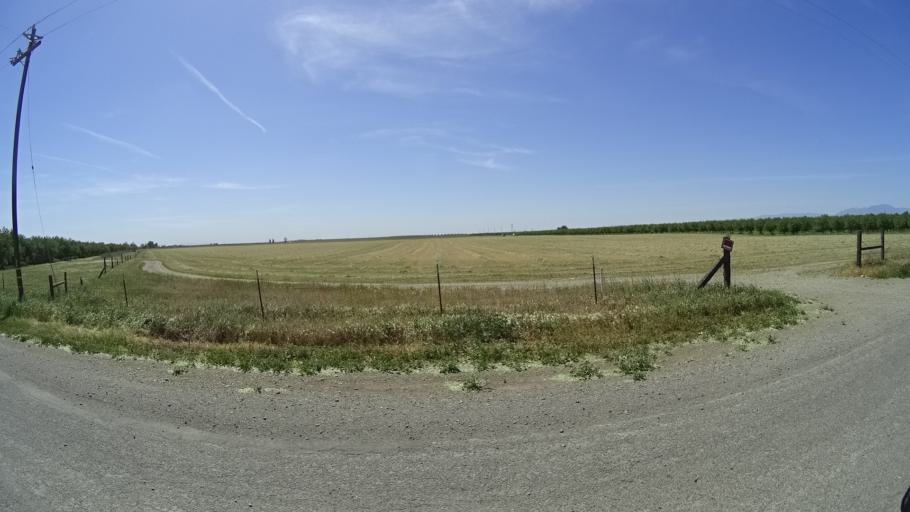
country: US
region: California
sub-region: Glenn County
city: Orland
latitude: 39.6530
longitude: -122.1679
